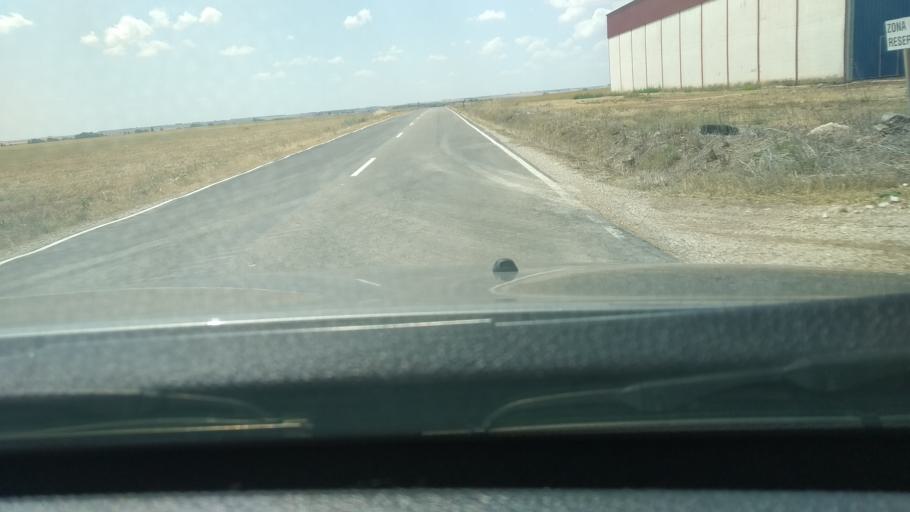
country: ES
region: Castille and Leon
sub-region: Provincia de Burgos
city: Villafruela
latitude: 41.9299
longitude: -3.8891
